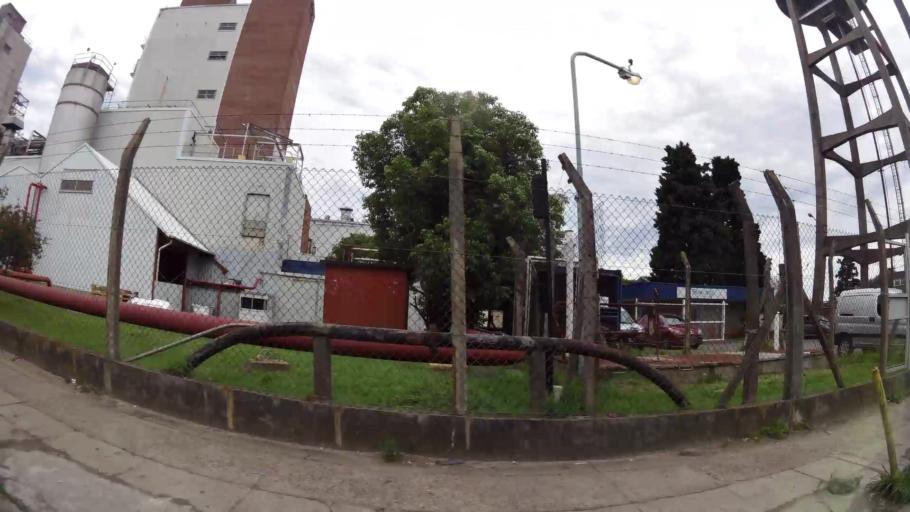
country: AR
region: Buenos Aires
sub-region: Partido de Quilmes
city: Quilmes
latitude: -34.7535
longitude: -58.2168
